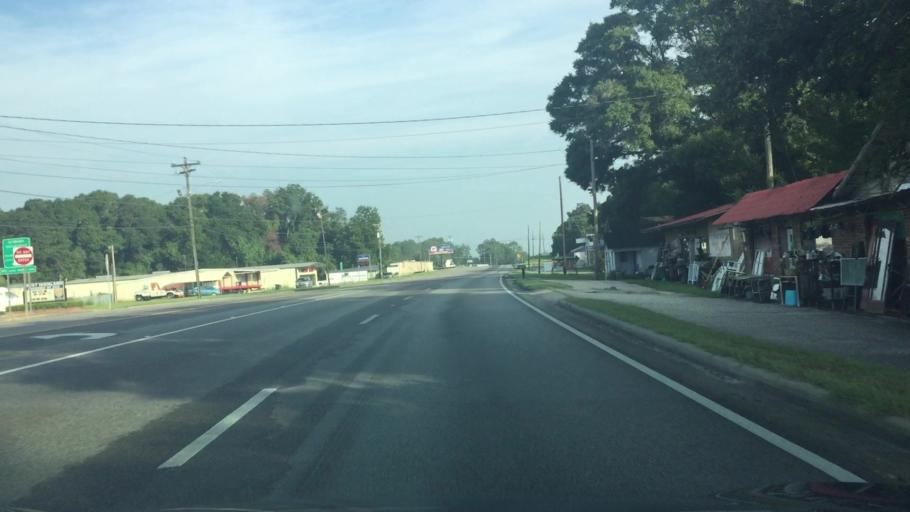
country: US
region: Alabama
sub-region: Covington County
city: Andalusia
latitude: 31.3225
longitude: -86.5053
